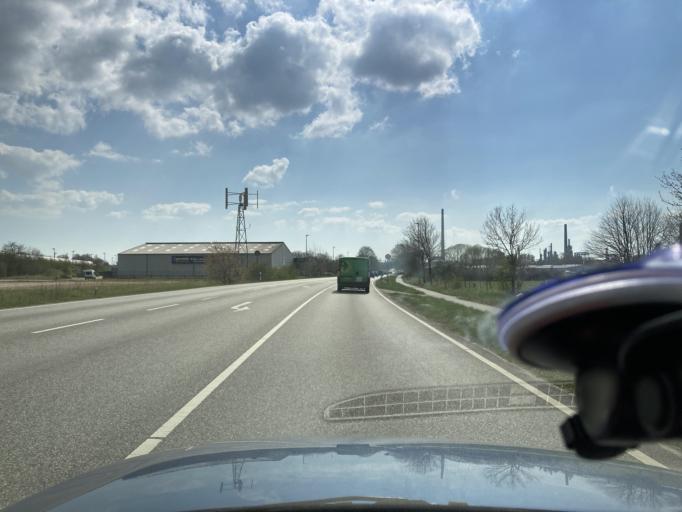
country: DE
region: Schleswig-Holstein
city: Hemmingstedt
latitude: 54.1673
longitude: 9.0900
